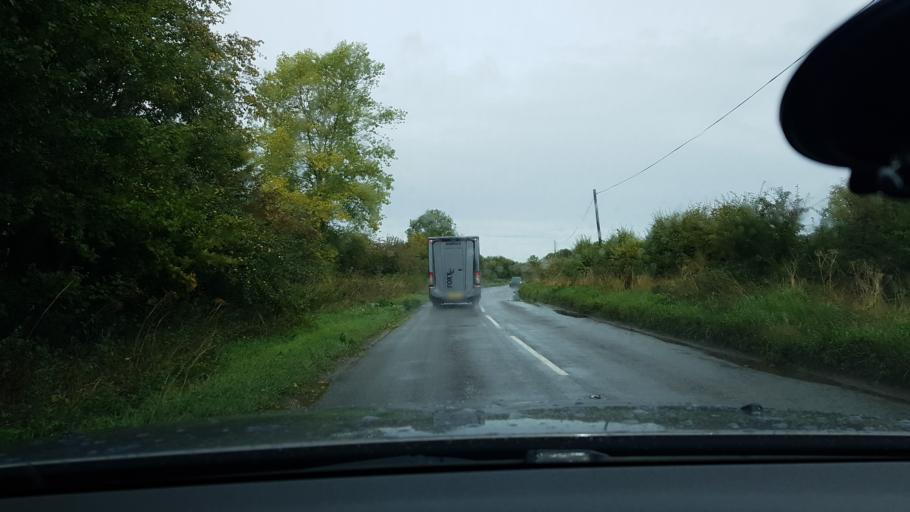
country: GB
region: England
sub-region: West Berkshire
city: Lambourn
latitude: 51.5180
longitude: -1.5232
